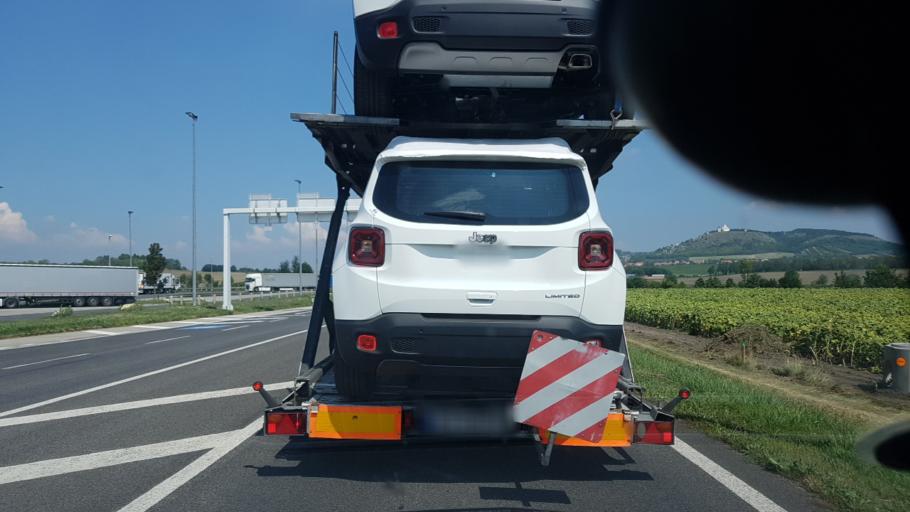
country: CZ
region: South Moravian
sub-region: Okres Breclav
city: Mikulov
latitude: 48.7811
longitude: 16.6399
